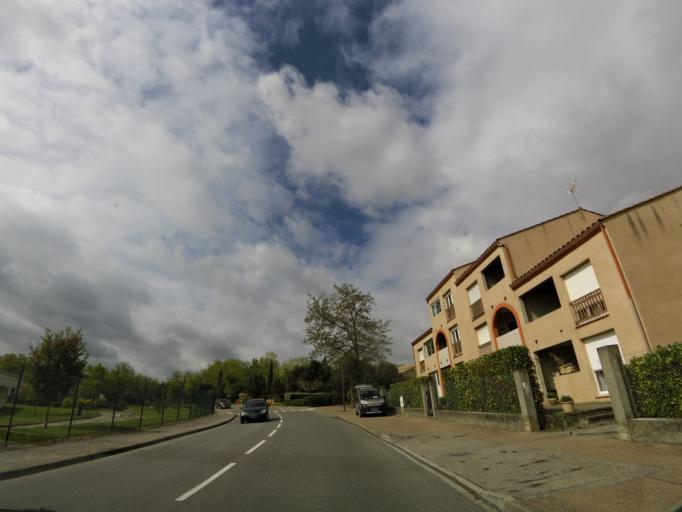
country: FR
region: Languedoc-Roussillon
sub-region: Departement de l'Aude
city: Castelnaudary
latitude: 43.3161
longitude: 1.9642
